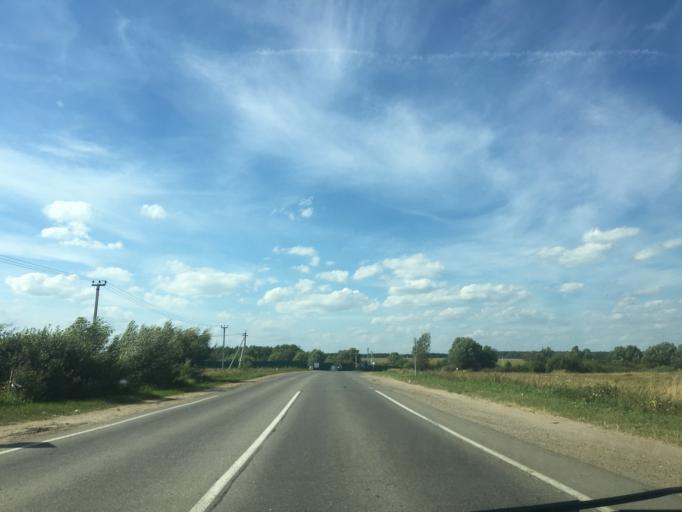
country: RU
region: Moskovskaya
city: Yam
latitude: 55.4775
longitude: 37.6652
